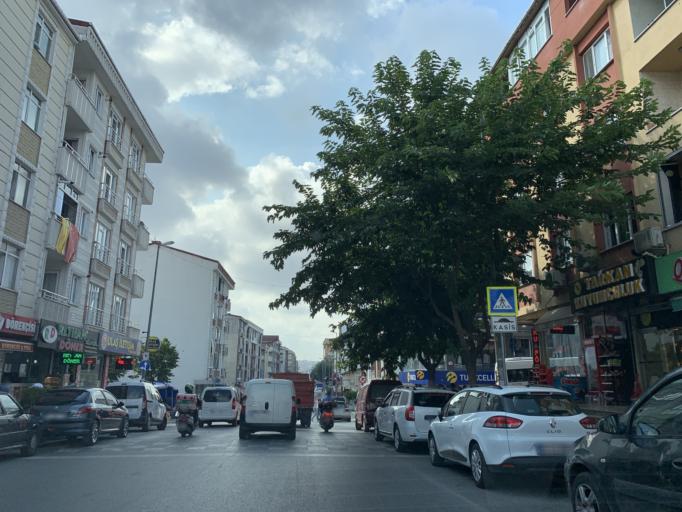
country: TR
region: Istanbul
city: Esenyurt
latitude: 41.0221
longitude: 28.6733
